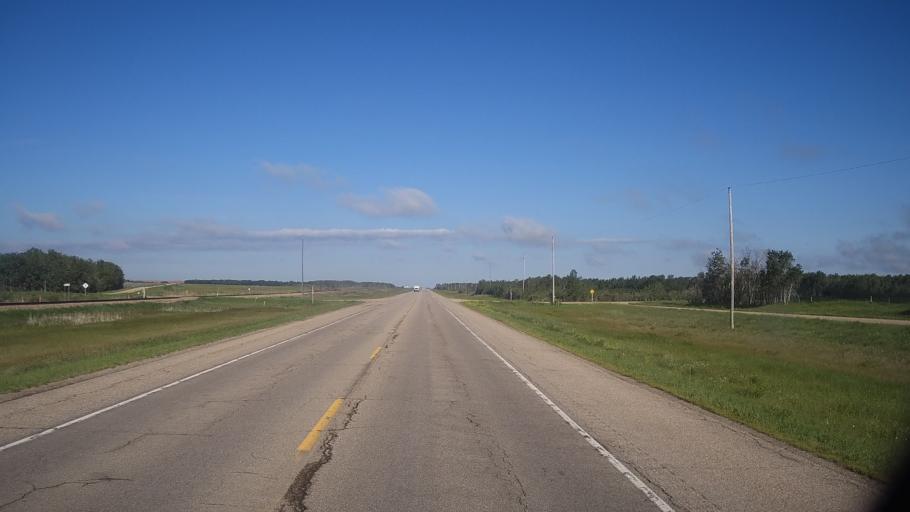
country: CA
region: Saskatchewan
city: Lanigan
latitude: 51.8528
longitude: -105.0739
